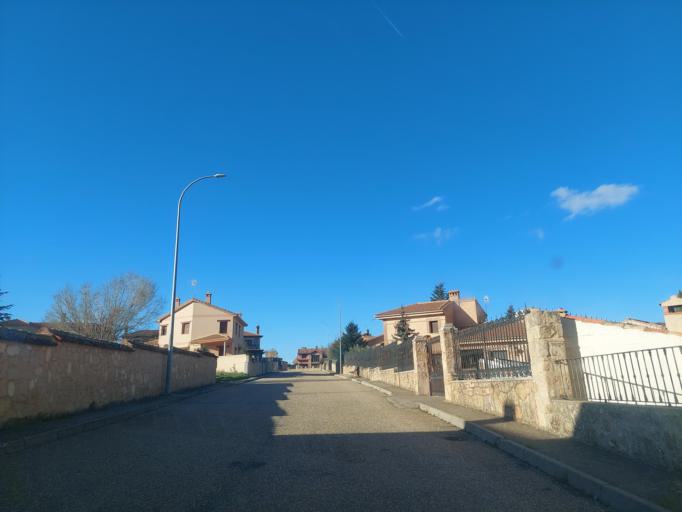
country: ES
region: Castille and Leon
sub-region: Provincia de Segovia
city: Pradena
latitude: 41.1342
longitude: -3.6915
